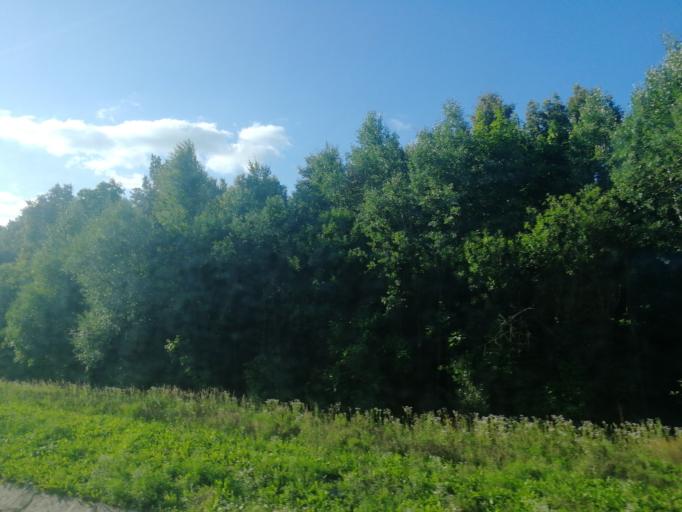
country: RU
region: Tula
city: Novogurovskiy
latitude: 54.2789
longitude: 37.2385
